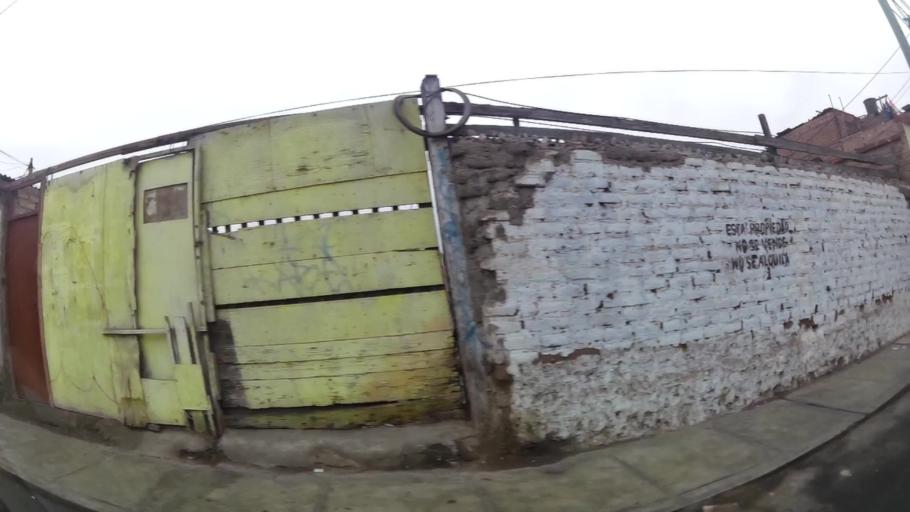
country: PE
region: Callao
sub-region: Callao
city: Callao
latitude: -12.0870
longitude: -77.0869
